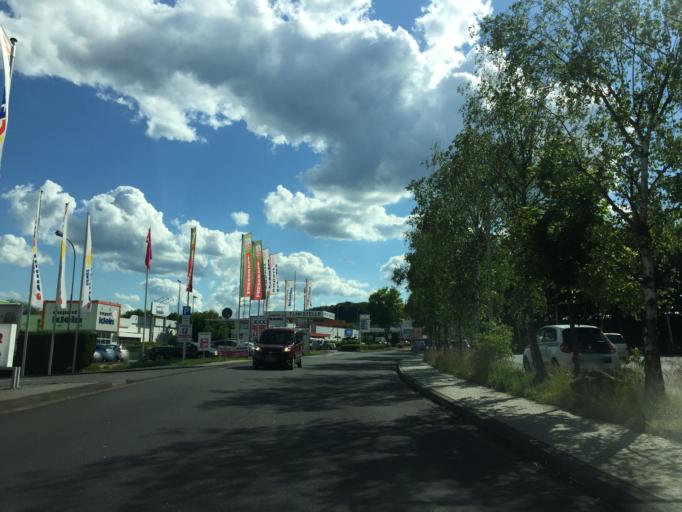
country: DE
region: Rheinland-Pfalz
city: Heiligenroth
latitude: 50.4501
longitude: 7.8532
